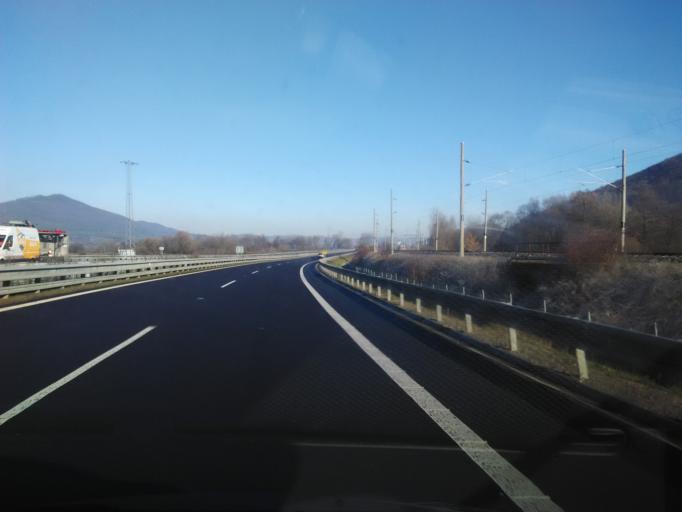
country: SK
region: Banskobystricky
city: Zarnovica
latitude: 48.5153
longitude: 18.7328
